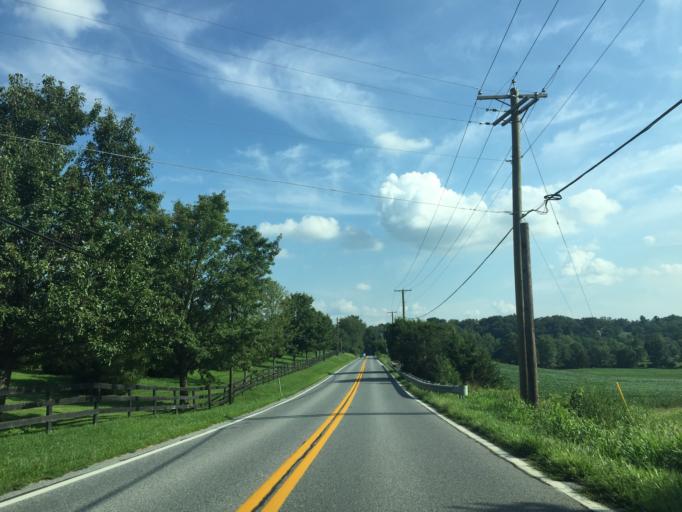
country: US
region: Maryland
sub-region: Carroll County
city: Hampstead
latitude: 39.6211
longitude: -76.7921
